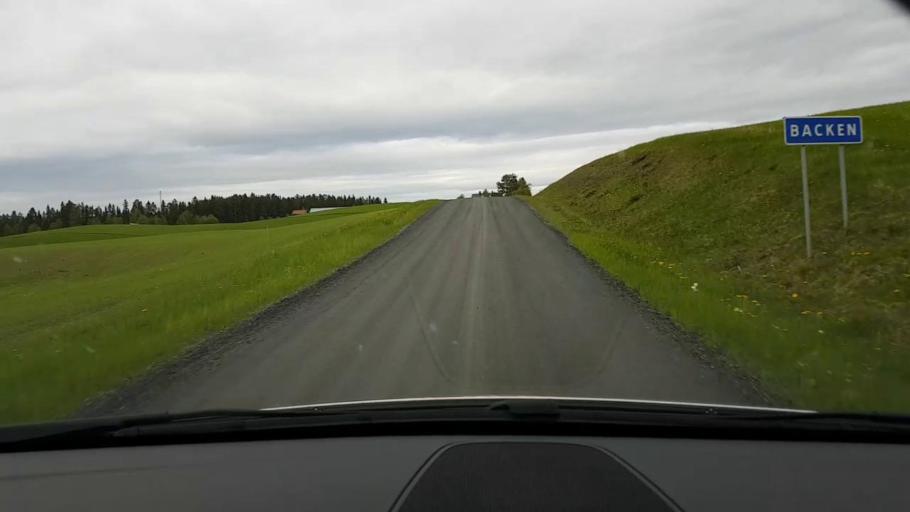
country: SE
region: Jaemtland
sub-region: Krokoms Kommun
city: Krokom
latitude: 63.3084
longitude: 14.3940
